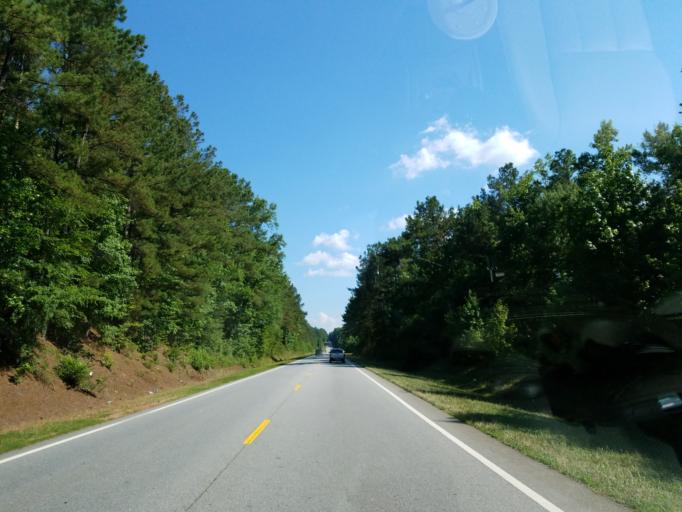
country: US
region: Georgia
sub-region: Crawford County
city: Roberta
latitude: 32.7763
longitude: -84.0218
